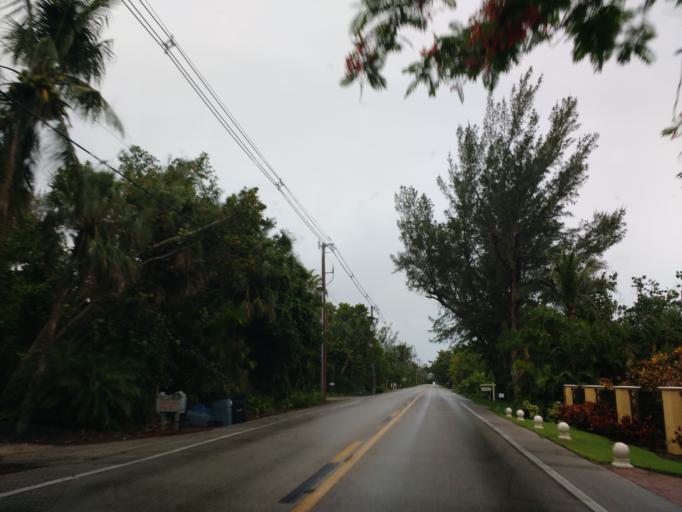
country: US
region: Florida
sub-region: Lee County
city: Saint James City
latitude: 26.4884
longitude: -82.1842
